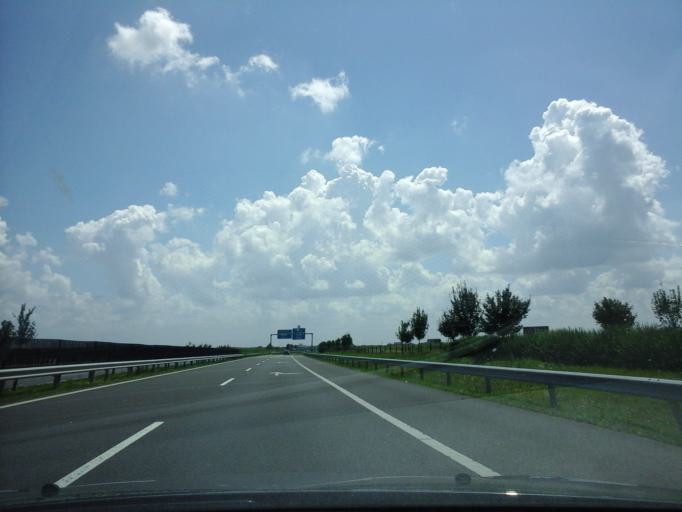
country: HU
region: Hajdu-Bihar
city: Hajduboszormeny
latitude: 47.5743
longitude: 21.5403
